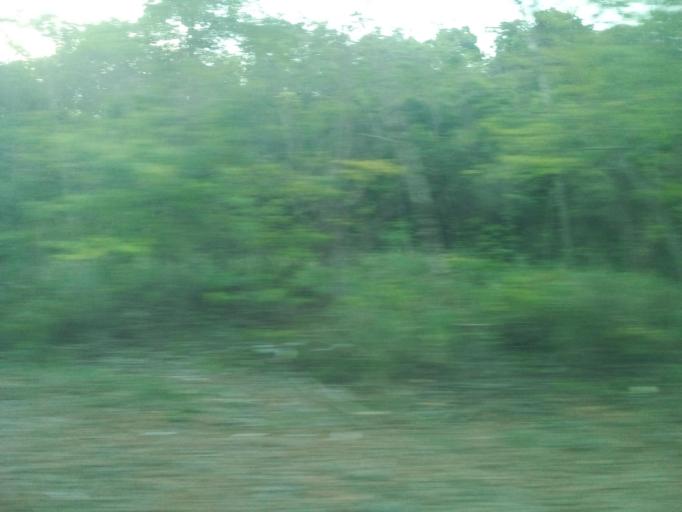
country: BR
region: Maranhao
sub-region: Imperatriz
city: Imperatriz
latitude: -4.8027
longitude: -47.3517
